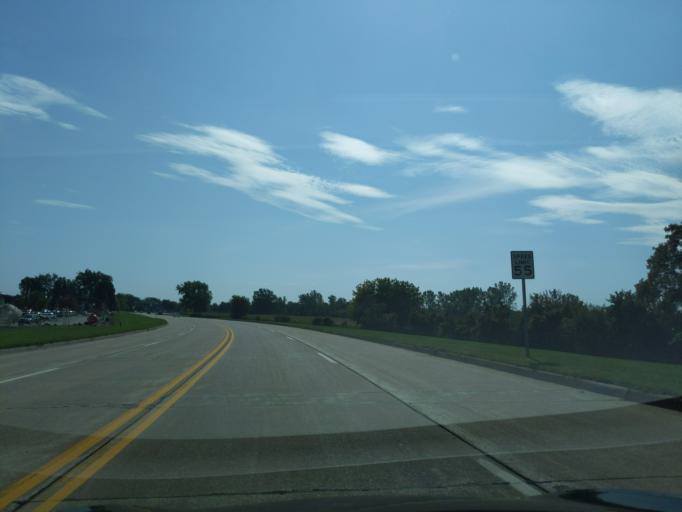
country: US
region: Michigan
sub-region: Saginaw County
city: Frankenmuth
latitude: 43.3149
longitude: -83.7399
